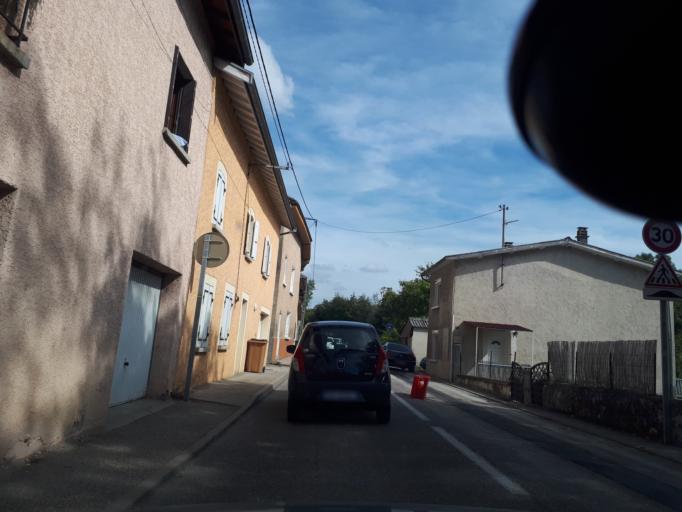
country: FR
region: Rhone-Alpes
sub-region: Departement de l'Isere
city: Chatonnay
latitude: 45.5149
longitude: 5.2022
